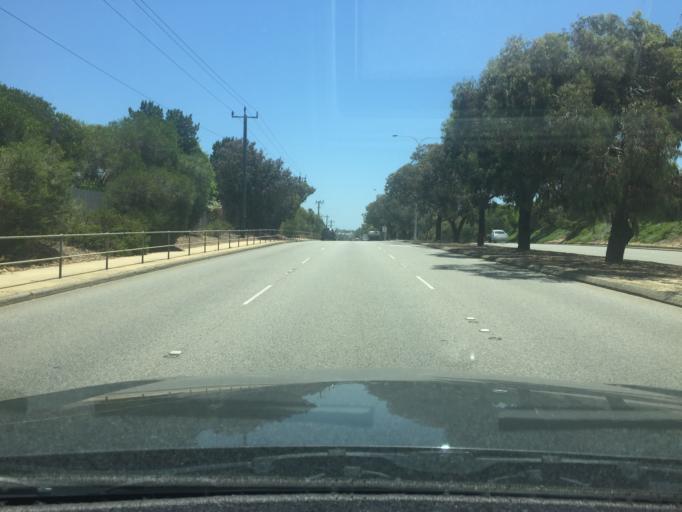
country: AU
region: Western Australia
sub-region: Melville
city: Kardinya
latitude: -32.0668
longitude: 115.8067
